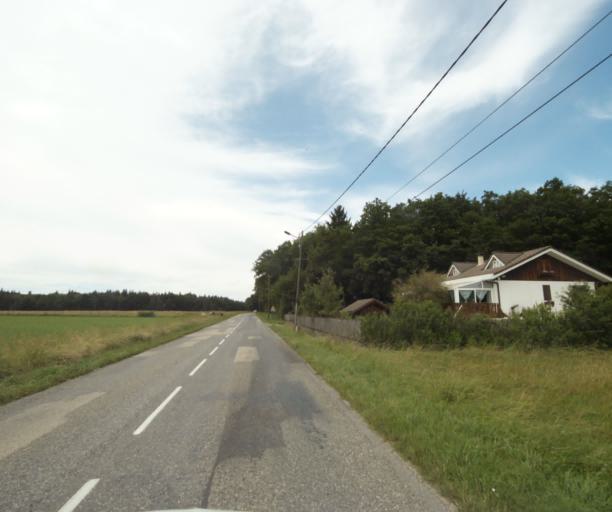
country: FR
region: Rhone-Alpes
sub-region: Departement de la Haute-Savoie
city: Perrignier
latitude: 46.3023
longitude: 6.4148
